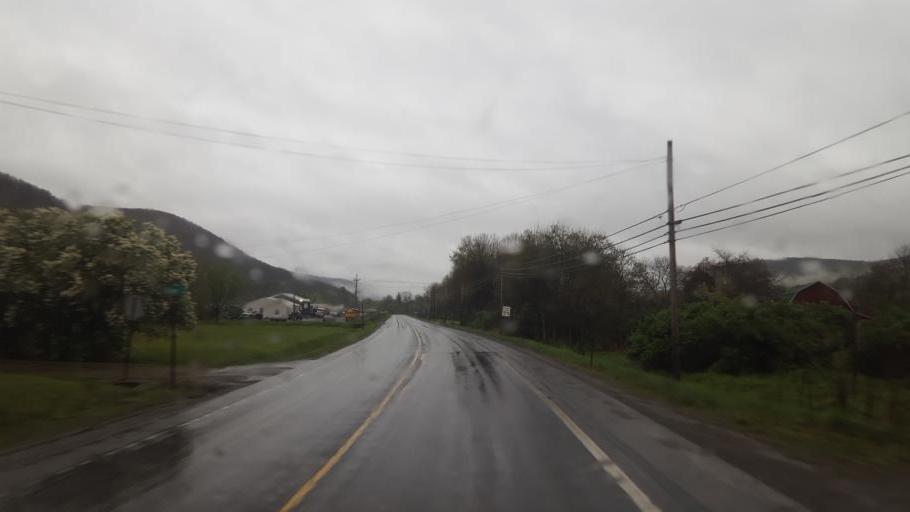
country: US
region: Pennsylvania
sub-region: Tioga County
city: Westfield
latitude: 41.9342
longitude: -77.4912
